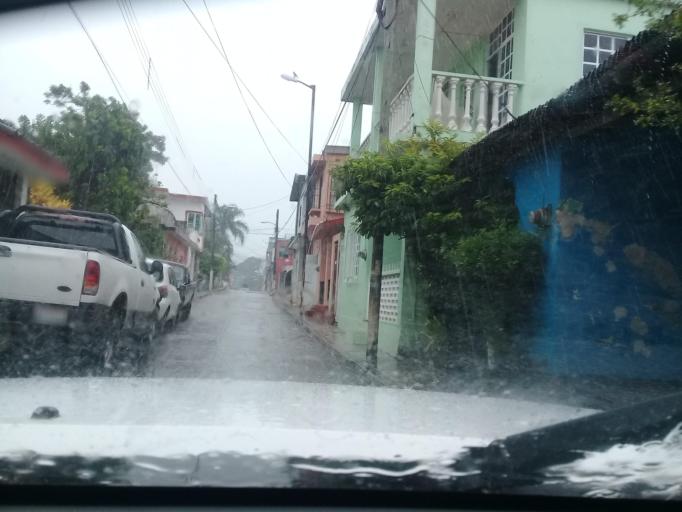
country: MX
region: Veracruz
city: Santiago Tuxtla
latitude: 18.4679
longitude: -95.3018
